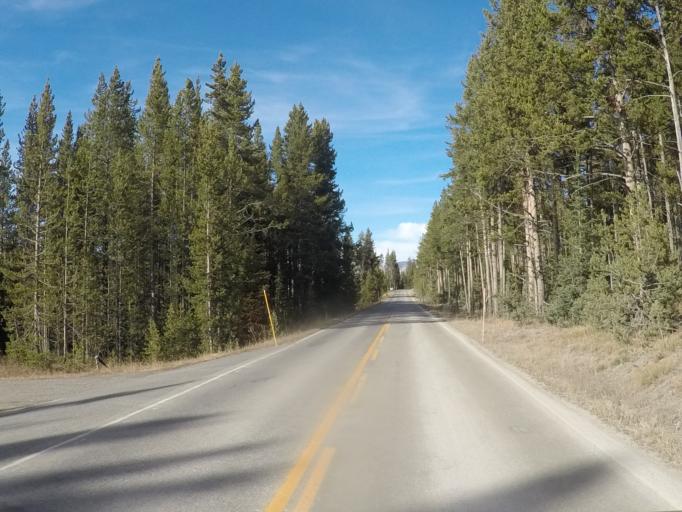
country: US
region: Montana
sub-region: Gallatin County
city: West Yellowstone
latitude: 44.8614
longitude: -110.7365
